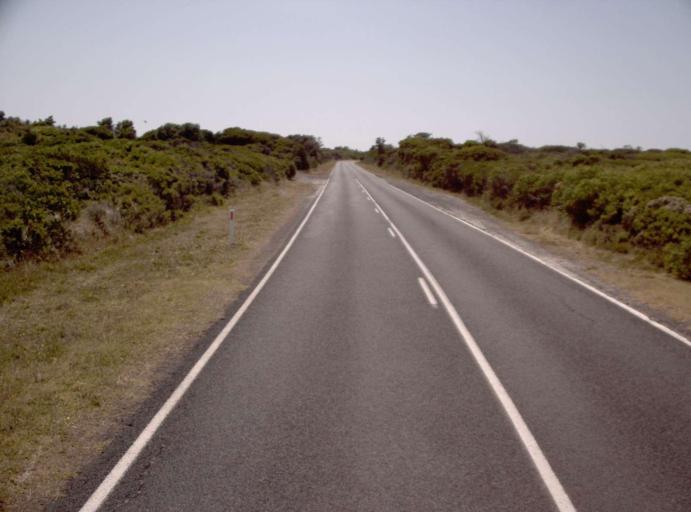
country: AU
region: Victoria
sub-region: Bass Coast
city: North Wonthaggi
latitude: -38.6726
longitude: 145.6304
